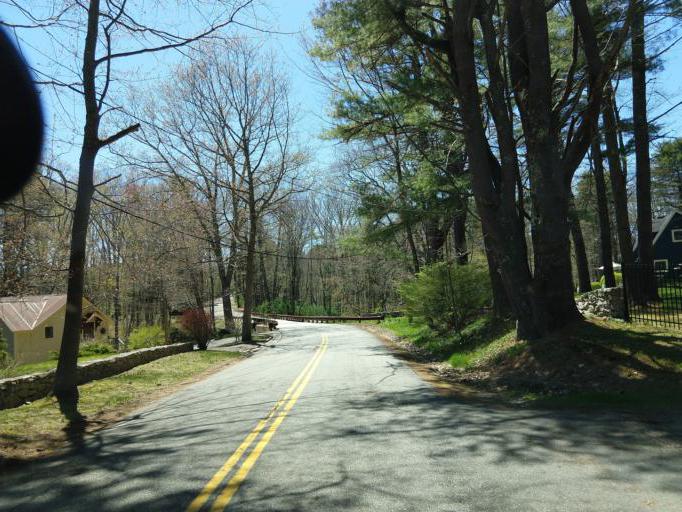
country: US
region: Maine
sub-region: York County
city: Kennebunk
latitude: 43.3455
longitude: -70.5528
